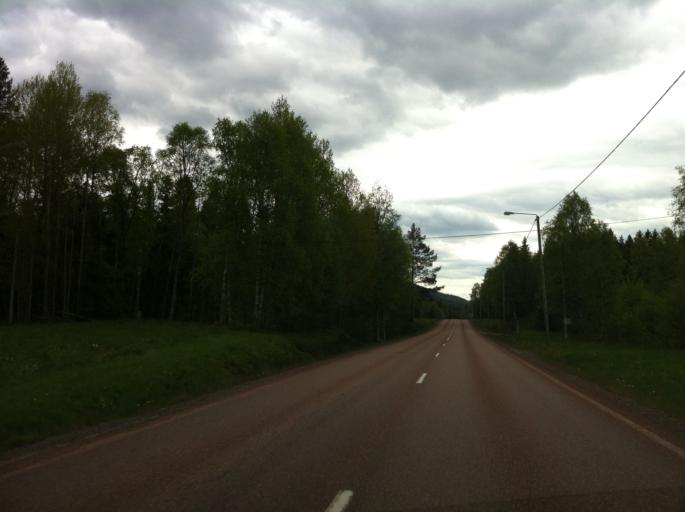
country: SE
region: Dalarna
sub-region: Malung-Saelens kommun
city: Malung
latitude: 61.0762
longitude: 13.3270
